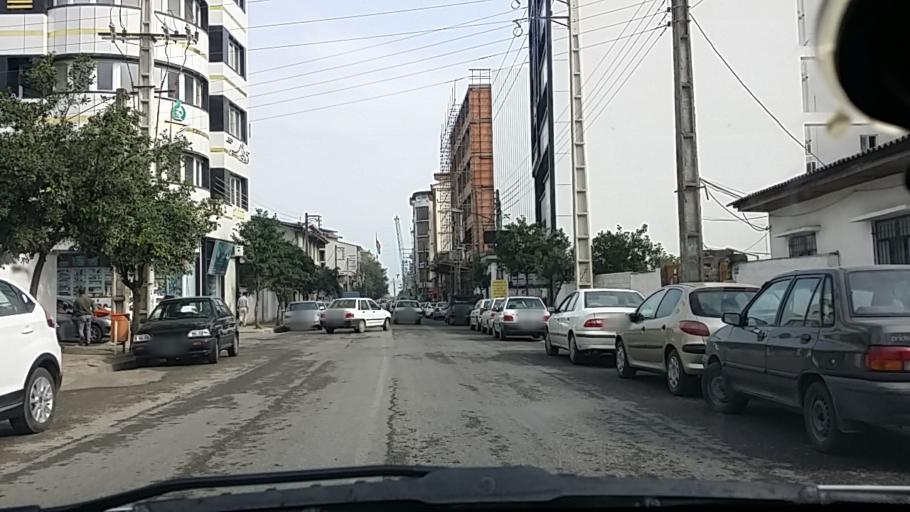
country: IR
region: Mazandaran
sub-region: Nowshahr
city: Nowshahr
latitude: 36.6487
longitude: 51.5086
